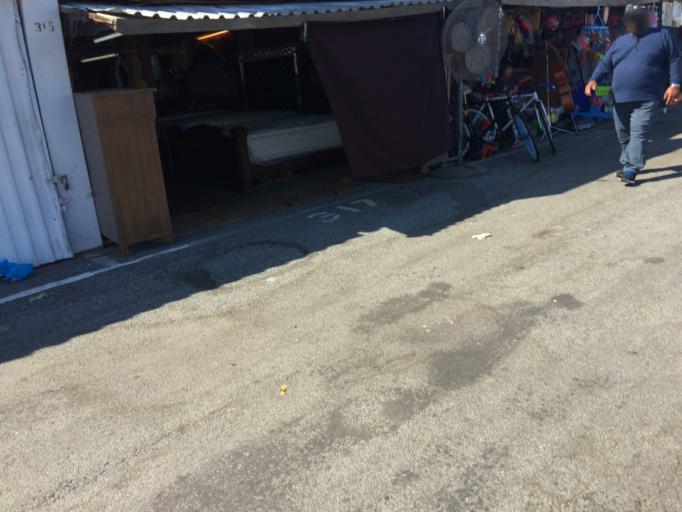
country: US
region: California
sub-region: Santa Clara County
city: San Jose
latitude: 37.3678
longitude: -121.8761
